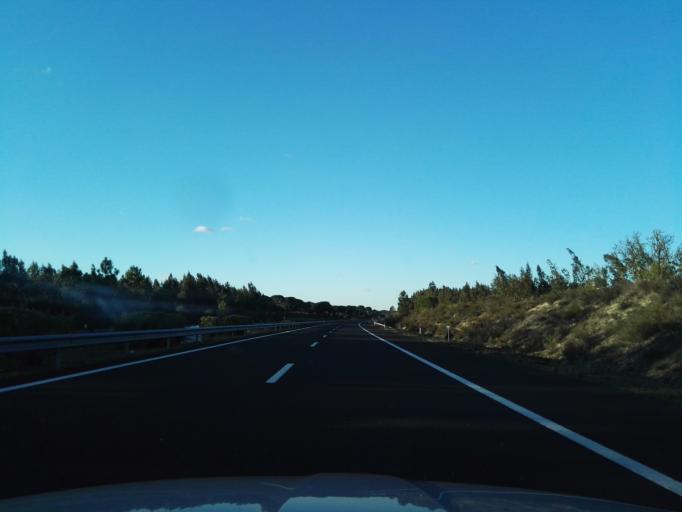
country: PT
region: Santarem
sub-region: Benavente
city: Poceirao
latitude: 38.7354
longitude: -8.6779
